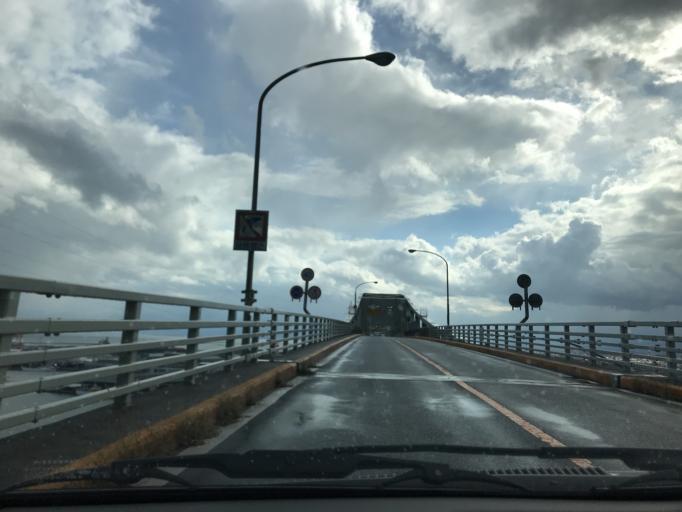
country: JP
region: Shimane
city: Sakaiminato
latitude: 35.5513
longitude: 133.2438
